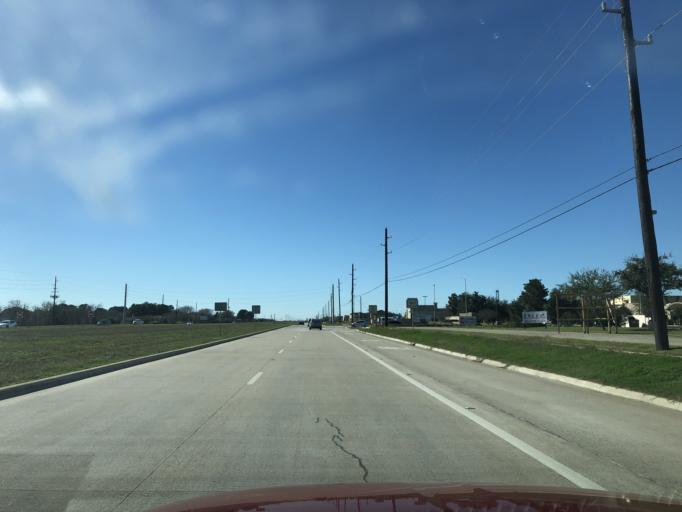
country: US
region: Texas
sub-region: Fort Bend County
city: Fulshear
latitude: 29.6960
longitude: -95.8334
